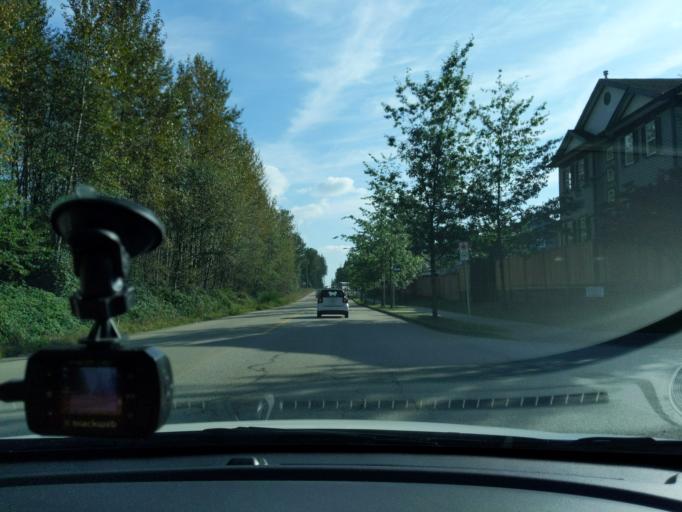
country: CA
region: British Columbia
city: Pitt Meadows
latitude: 49.2047
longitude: -122.6783
